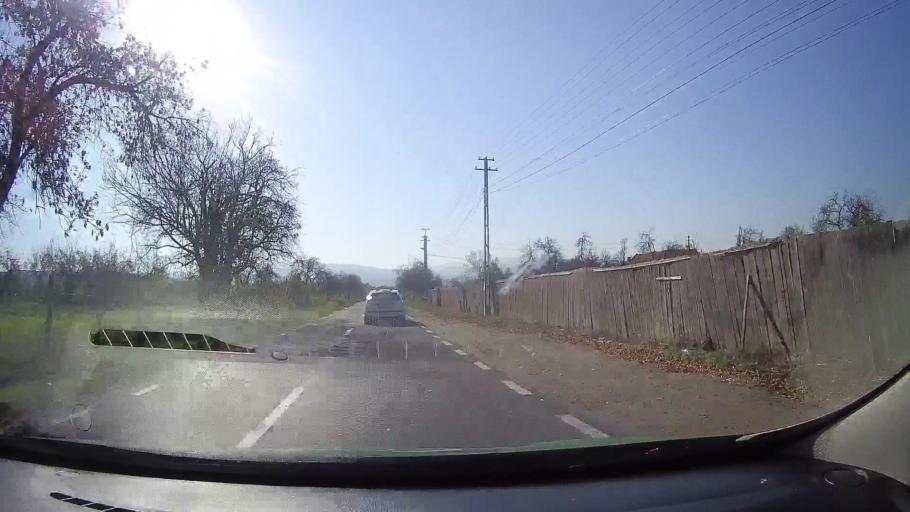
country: RO
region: Timis
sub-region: Comuna Curtea
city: Curtea
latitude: 45.8481
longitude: 22.3133
